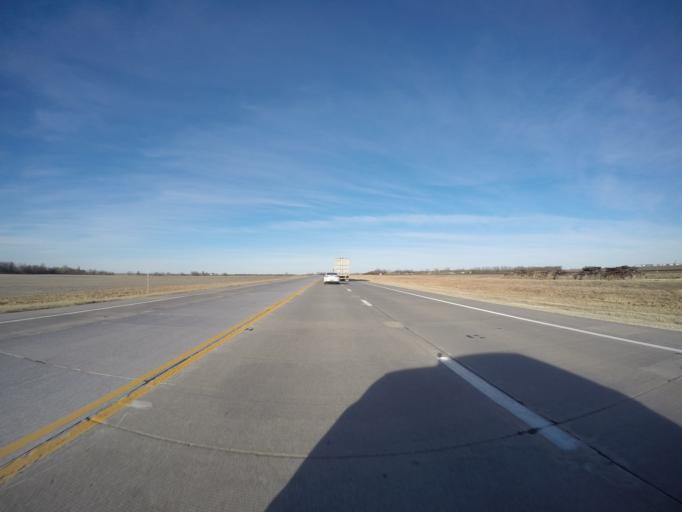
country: US
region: Kansas
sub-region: Harvey County
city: North Newton
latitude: 38.0882
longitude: -97.2885
